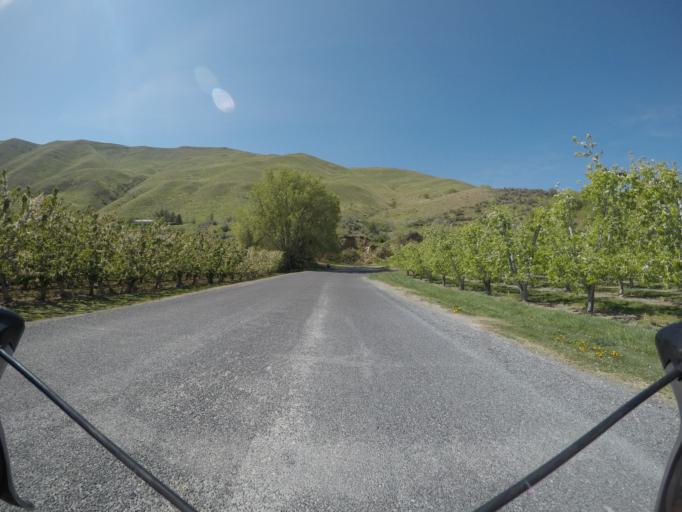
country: US
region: Washington
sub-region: Chelan County
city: West Wenatchee
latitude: 47.4709
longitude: -120.3787
